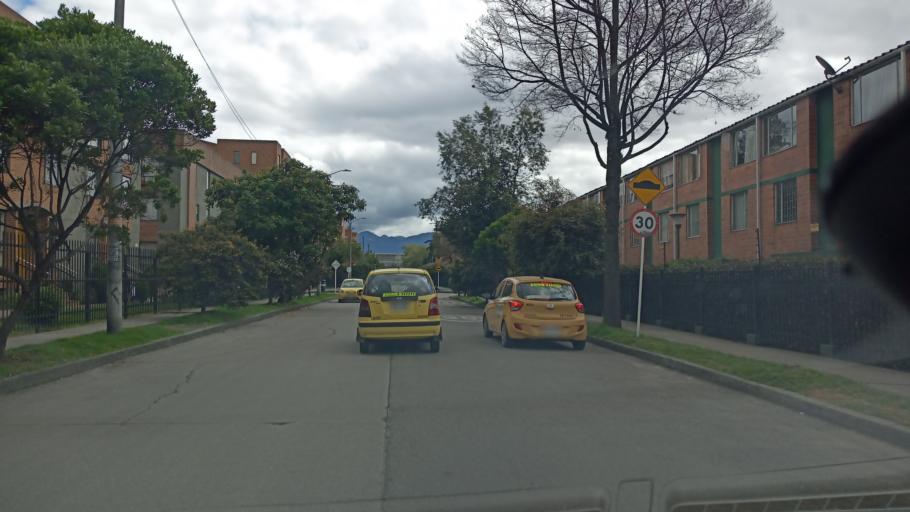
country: CO
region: Bogota D.C.
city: Bogota
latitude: 4.6672
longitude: -74.1335
